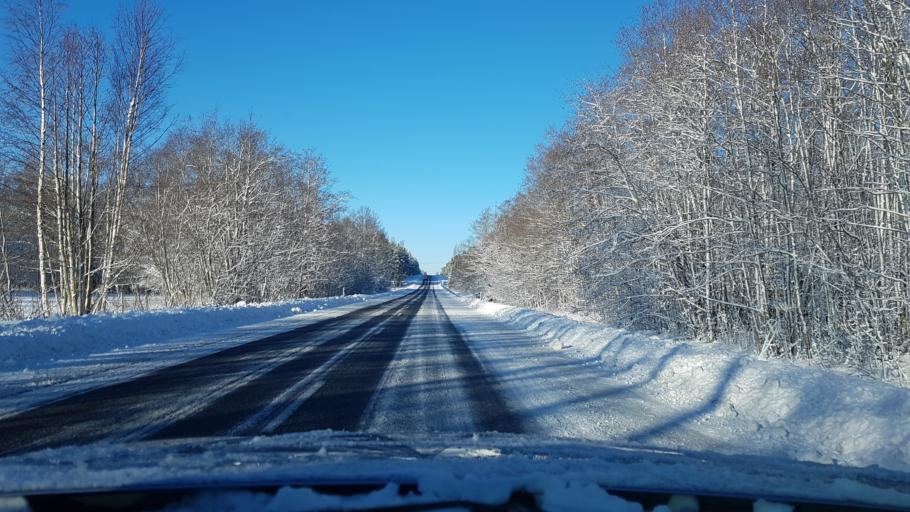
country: EE
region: Hiiumaa
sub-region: Kaerdla linn
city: Kardla
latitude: 58.9573
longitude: 22.8610
